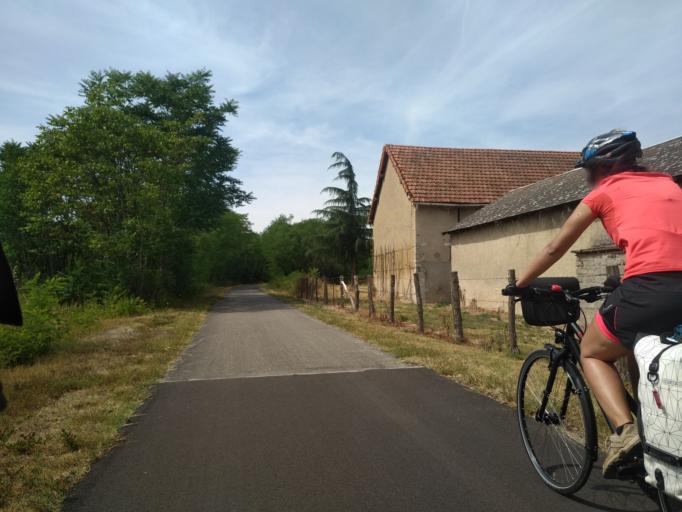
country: FR
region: Auvergne
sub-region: Departement de l'Allier
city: Diou
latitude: 46.5419
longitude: 3.7480
